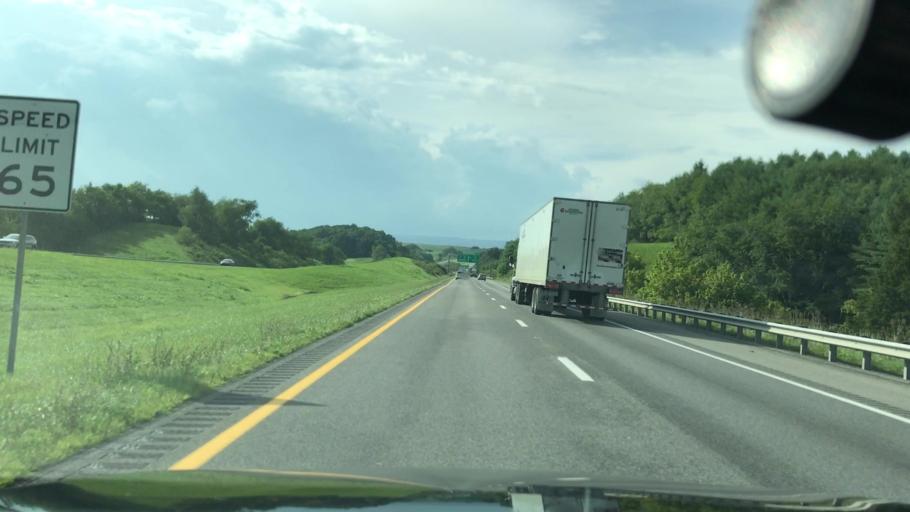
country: US
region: Virginia
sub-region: Pulaski County
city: Pulaski
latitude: 36.9217
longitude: -80.9010
